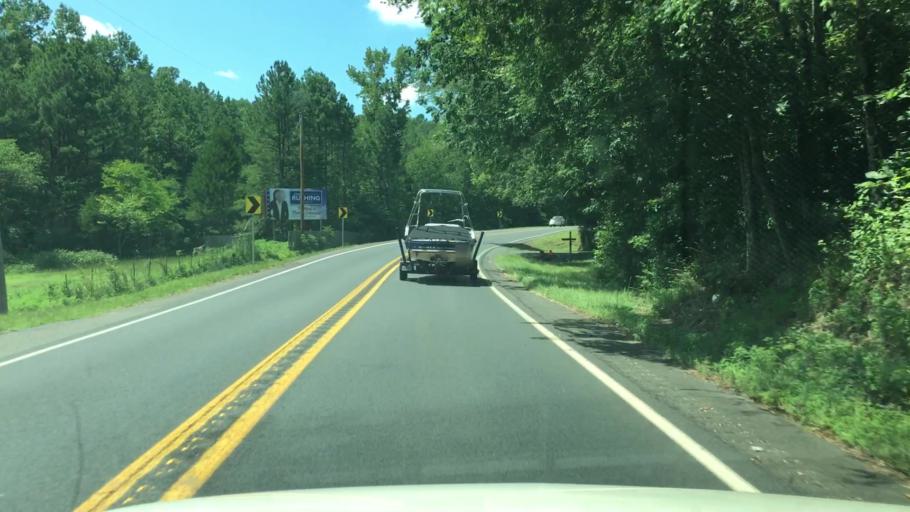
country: US
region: Arkansas
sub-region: Garland County
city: Lake Hamilton
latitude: 34.3396
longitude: -93.1823
